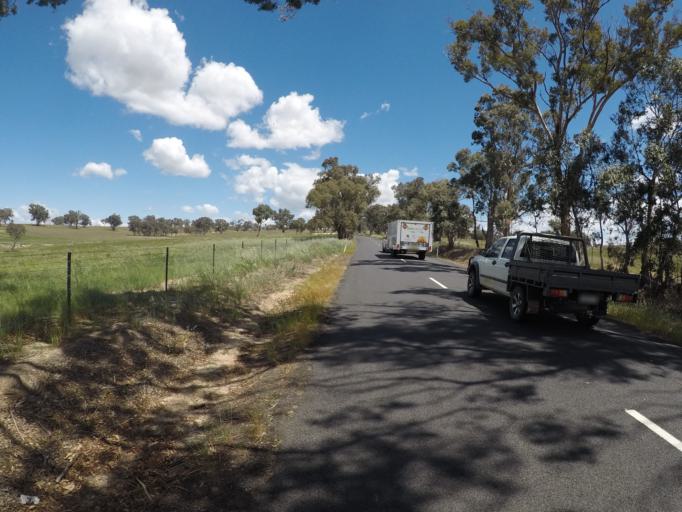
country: AU
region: New South Wales
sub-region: Bathurst Regional
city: Perthville
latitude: -33.5259
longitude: 149.4737
